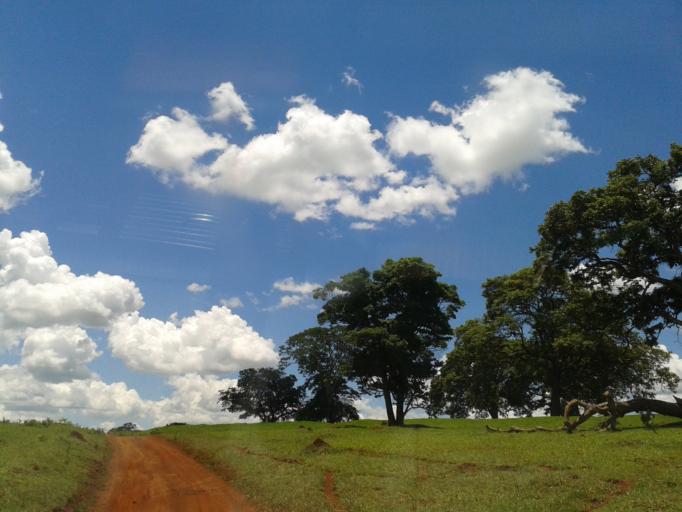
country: BR
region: Minas Gerais
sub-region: Centralina
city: Centralina
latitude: -18.6981
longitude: -49.1851
